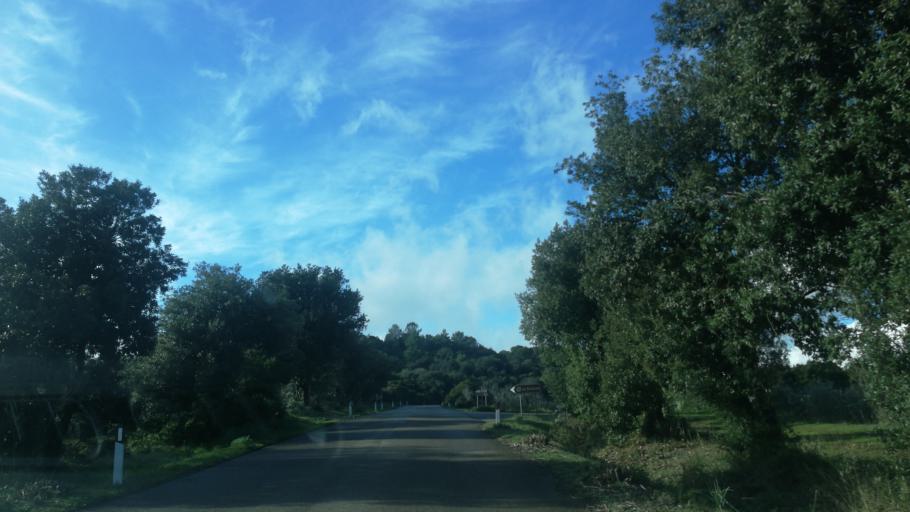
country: IT
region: Sardinia
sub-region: Provincia di Medio Campidano
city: Villanovaforru
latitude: 39.6338
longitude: 8.8590
